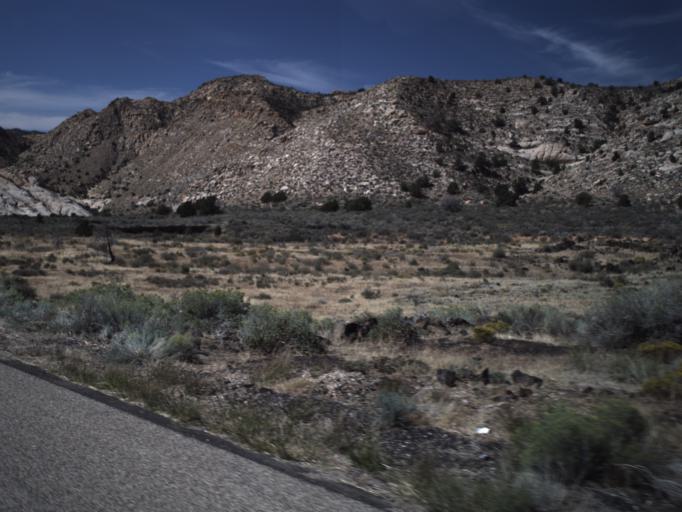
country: US
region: Utah
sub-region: Washington County
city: Ivins
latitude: 37.2453
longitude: -113.6308
